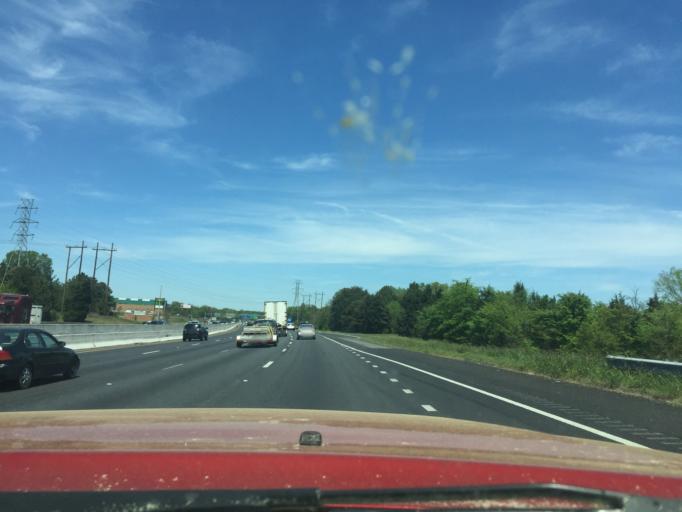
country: US
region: North Carolina
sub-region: Mecklenburg County
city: Pineville
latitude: 35.0935
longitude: -80.9326
